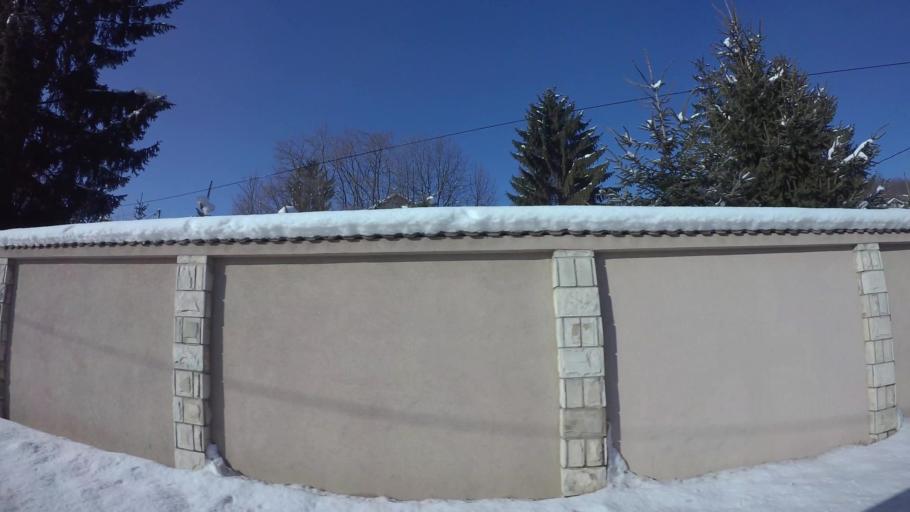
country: BA
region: Federation of Bosnia and Herzegovina
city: Kobilja Glava
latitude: 43.8834
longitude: 18.4154
